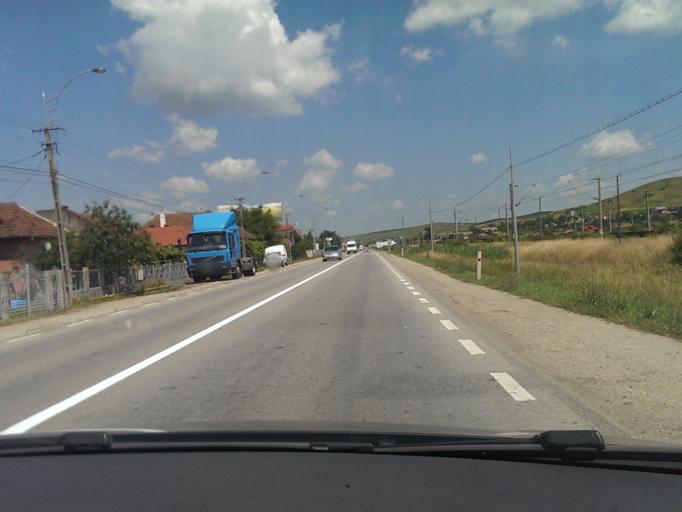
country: RO
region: Cluj
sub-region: Comuna Apahida
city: Sannicoara
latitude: 46.7847
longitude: 23.7198
